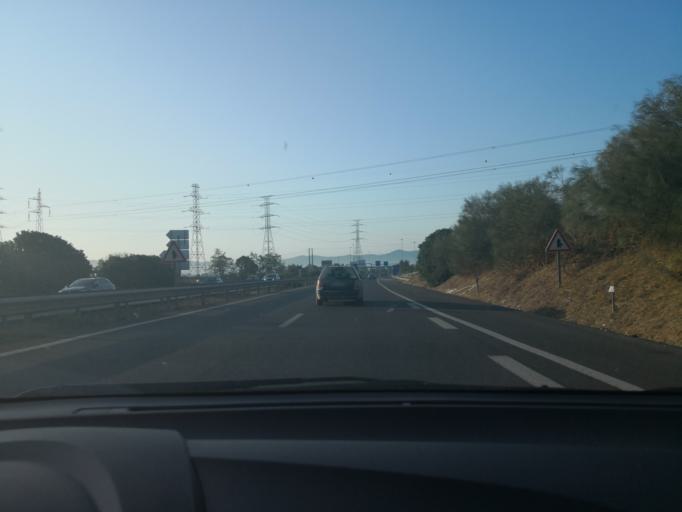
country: PT
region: Setubal
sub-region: Barreiro
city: Santo Antonio da Charneca
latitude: 38.5875
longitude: -9.0187
